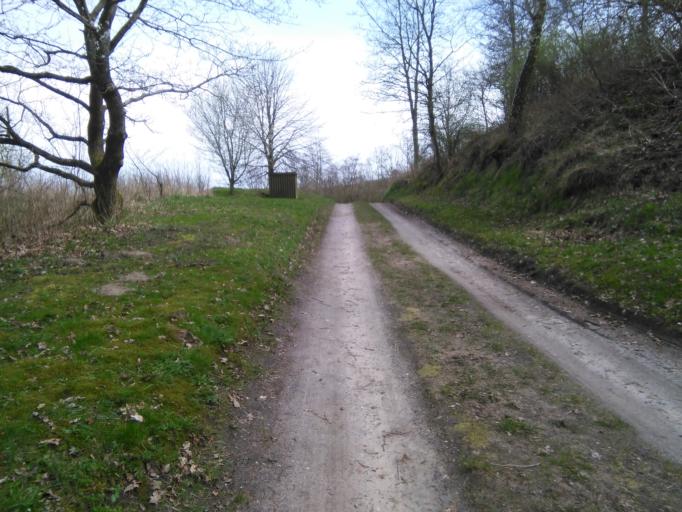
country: DK
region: Central Jutland
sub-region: Odder Kommune
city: Odder
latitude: 55.8853
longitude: 10.1203
